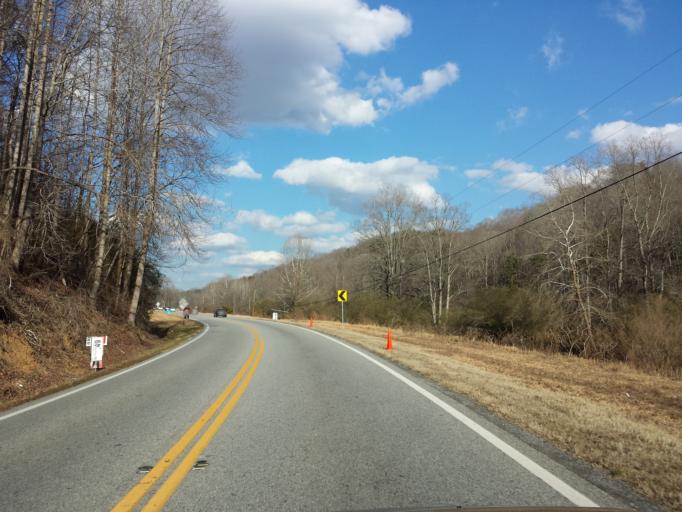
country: US
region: Georgia
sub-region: Lumpkin County
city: Dahlonega
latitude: 34.4852
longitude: -83.9524
